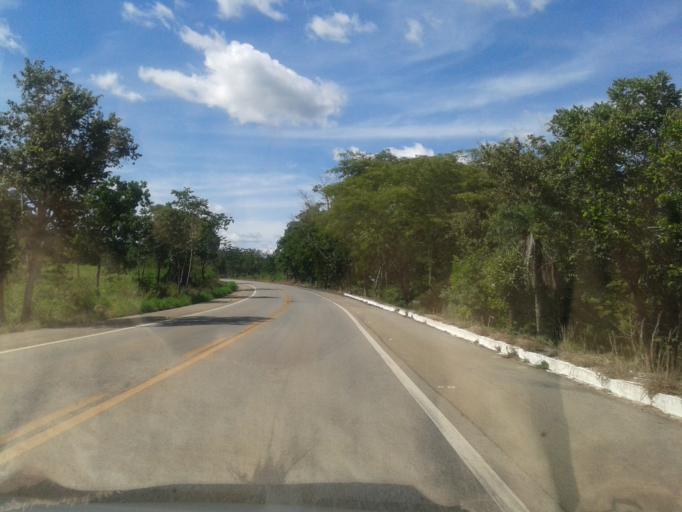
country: BR
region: Goias
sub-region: Itapuranga
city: Itapuranga
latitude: -15.4075
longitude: -50.3785
